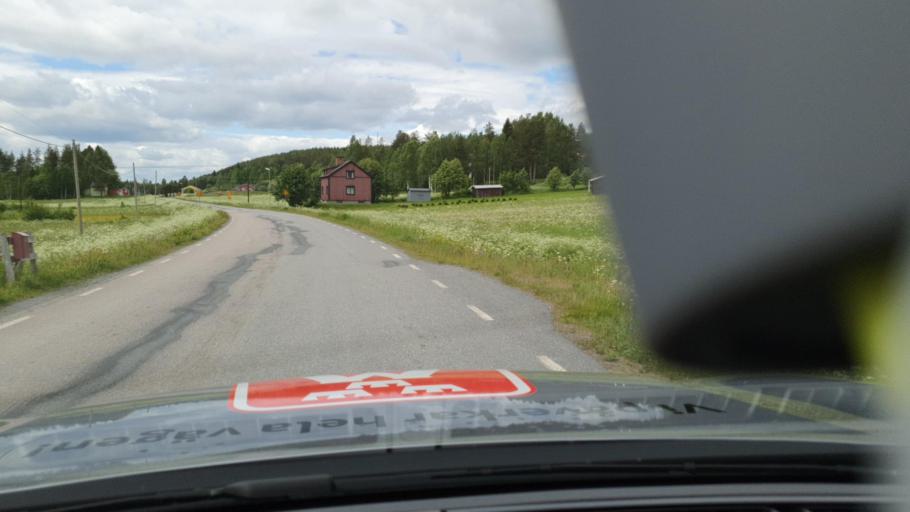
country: SE
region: Norrbotten
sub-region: Bodens Kommun
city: Saevast
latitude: 65.8703
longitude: 21.8931
